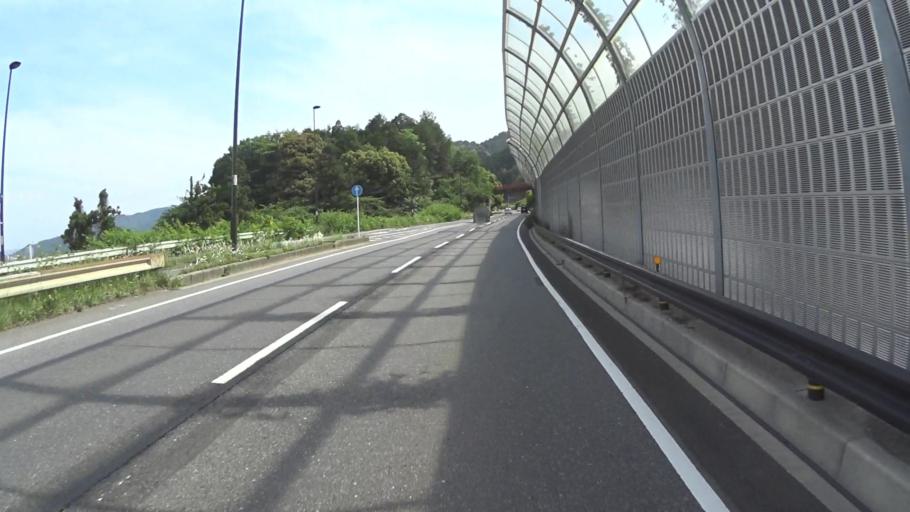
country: JP
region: Shiga Prefecture
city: Otsu-shi
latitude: 35.0253
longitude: 135.8501
